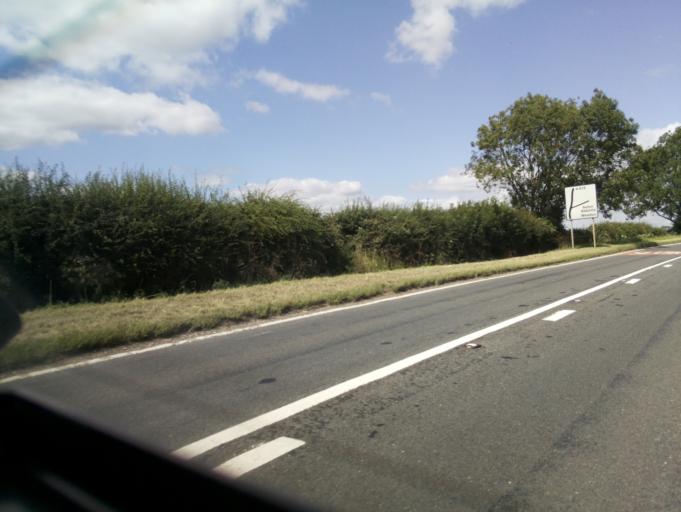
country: GB
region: England
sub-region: Buckinghamshire
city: Aylesbury
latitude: 51.8502
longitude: -0.8273
